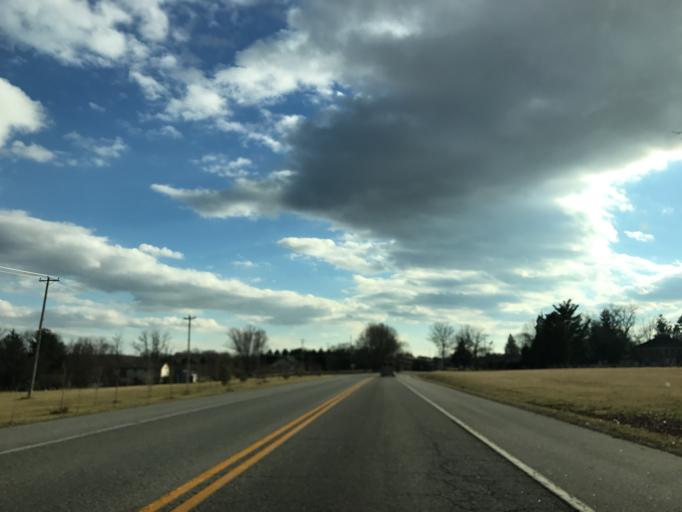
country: US
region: Maryland
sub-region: Cecil County
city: Rising Sun
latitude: 39.6720
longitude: -76.0740
